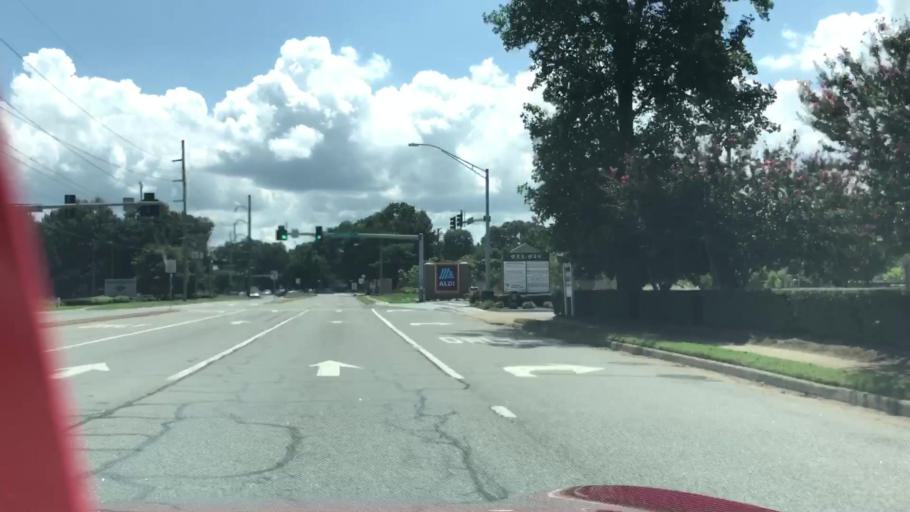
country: US
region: Virginia
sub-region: City of Virginia Beach
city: Virginia Beach
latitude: 36.8577
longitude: -76.0260
